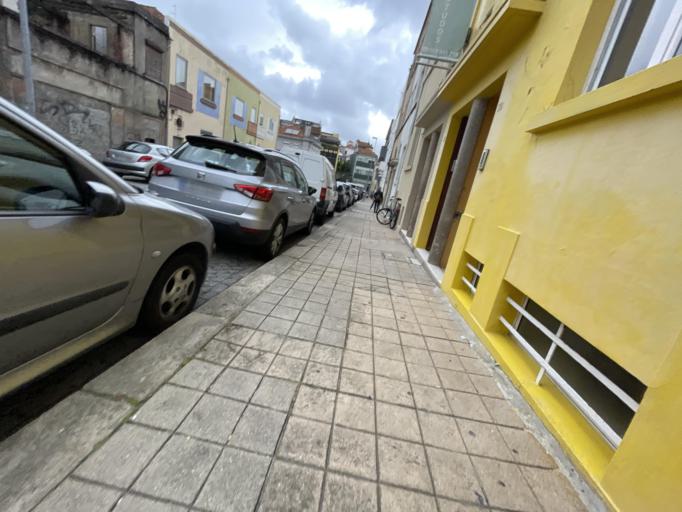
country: PT
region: Porto
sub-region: Porto
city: Porto
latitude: 41.1668
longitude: -8.6100
